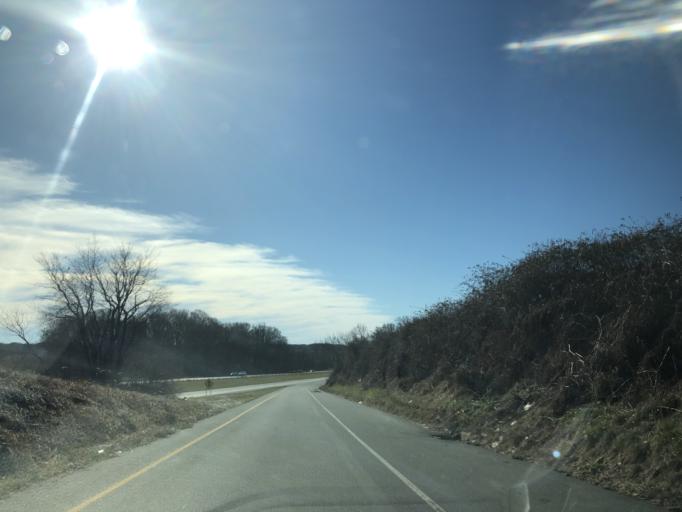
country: US
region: Pennsylvania
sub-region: Chester County
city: Oxford
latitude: 39.7878
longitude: -75.9972
